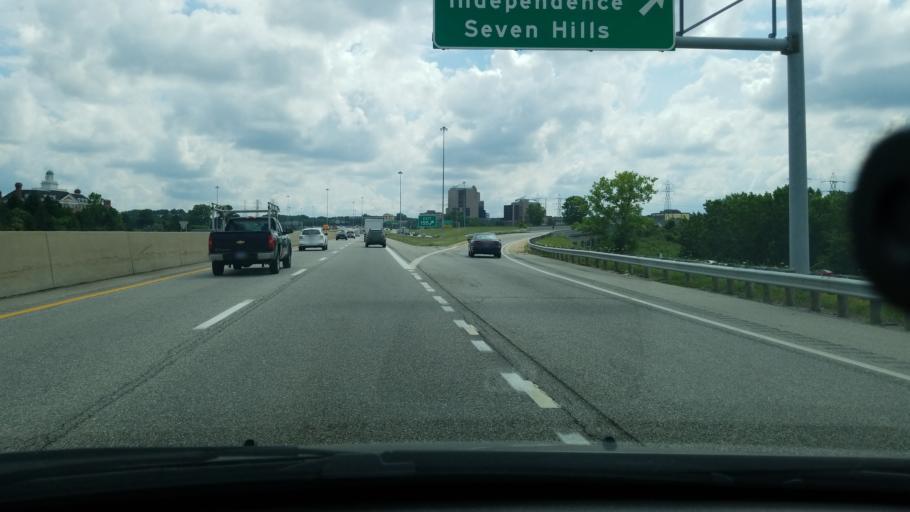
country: US
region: Ohio
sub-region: Cuyahoga County
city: Seven Hills
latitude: 41.4051
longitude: -81.6482
